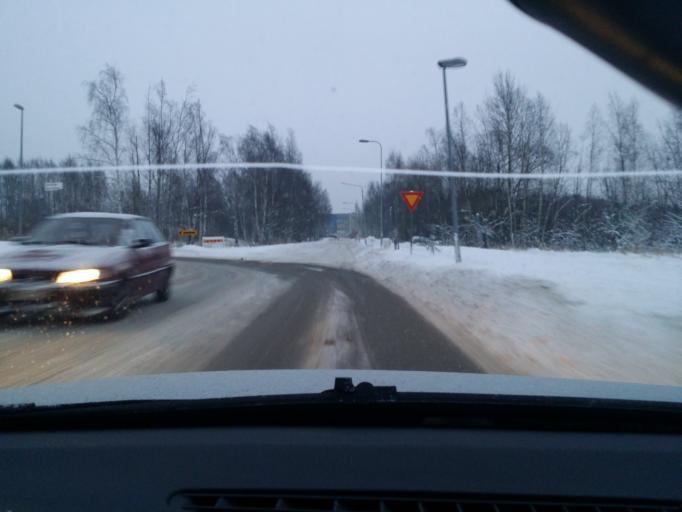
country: FI
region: Uusimaa
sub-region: Helsinki
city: Teekkarikylae
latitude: 60.2151
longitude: 24.8317
